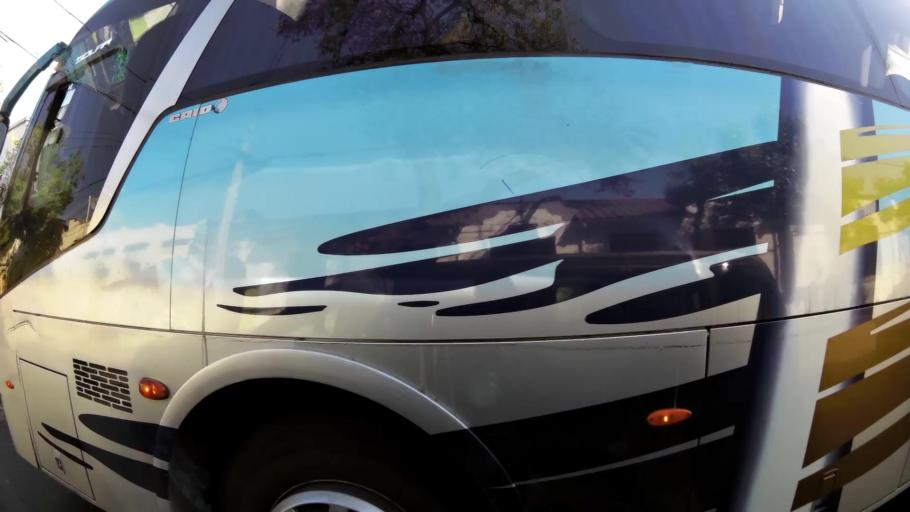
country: CL
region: Santiago Metropolitan
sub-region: Provincia de Santiago
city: Santiago
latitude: -33.4330
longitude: -70.6387
